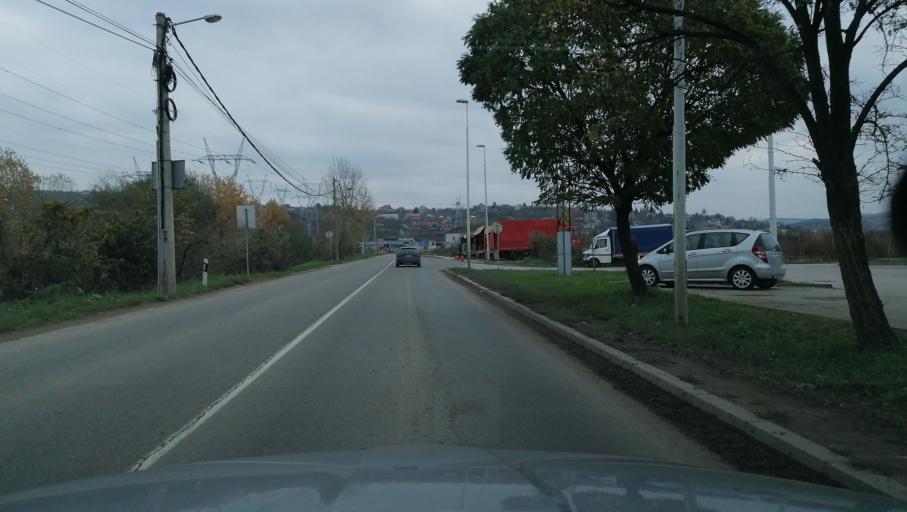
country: RS
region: Central Serbia
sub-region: Belgrade
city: Zvezdara
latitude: 44.7443
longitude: 20.6022
